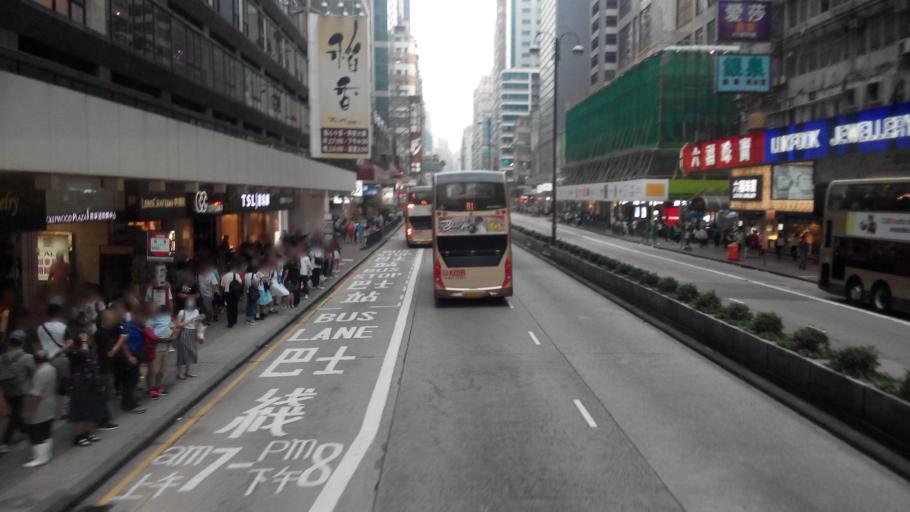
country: HK
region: Kowloon City
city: Kowloon
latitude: 22.3172
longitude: 114.1697
